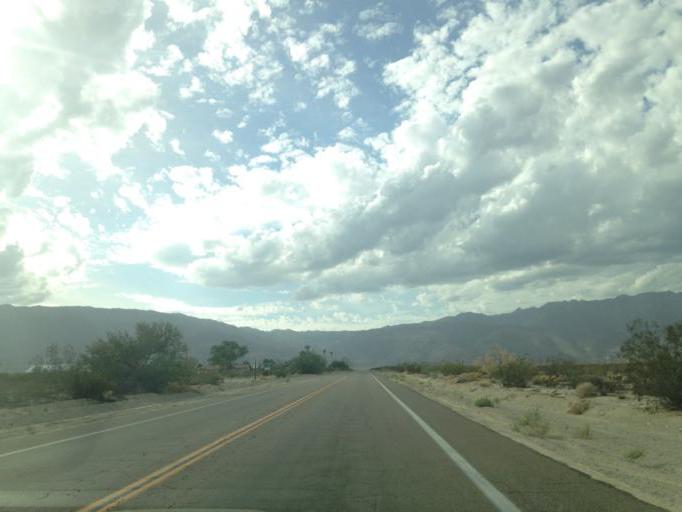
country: US
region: California
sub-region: San Diego County
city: Borrego Springs
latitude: 33.2112
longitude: -116.3362
